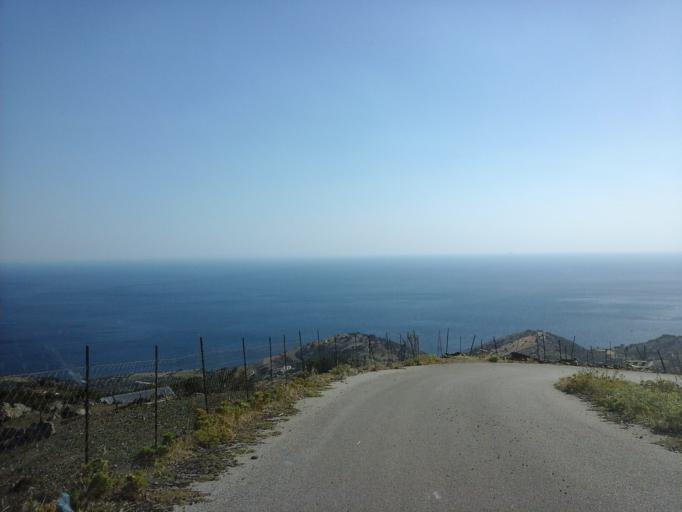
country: GR
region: East Macedonia and Thrace
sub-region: Nomos Evrou
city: Samothraki
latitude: 40.4307
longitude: 25.5440
